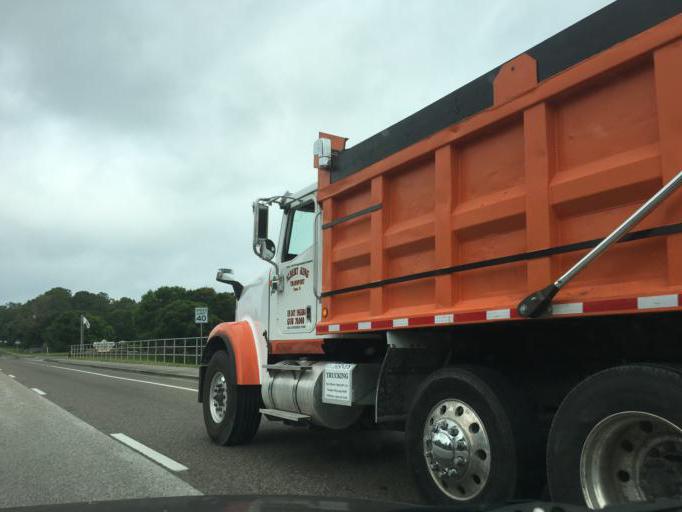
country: US
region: Florida
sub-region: Pinellas County
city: Dunedin
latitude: 28.0007
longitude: -82.7632
